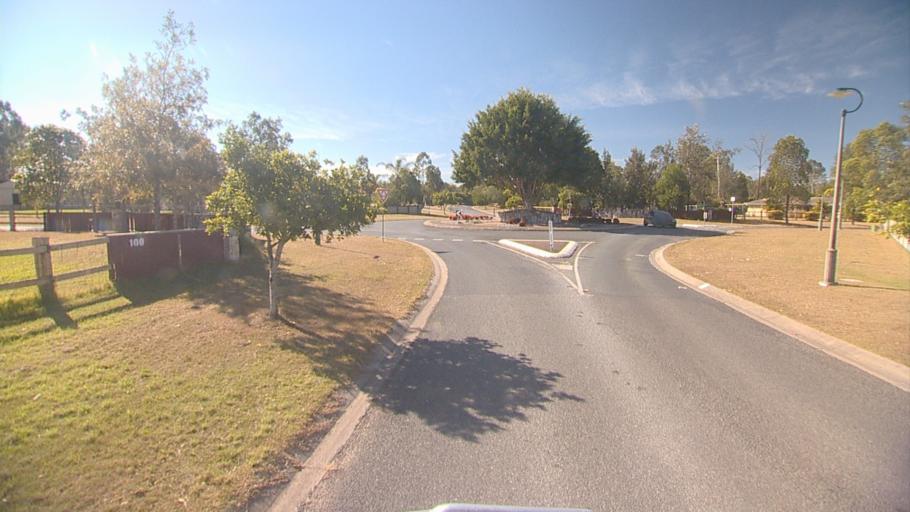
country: AU
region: Queensland
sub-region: Logan
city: North Maclean
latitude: -27.8024
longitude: 152.9670
